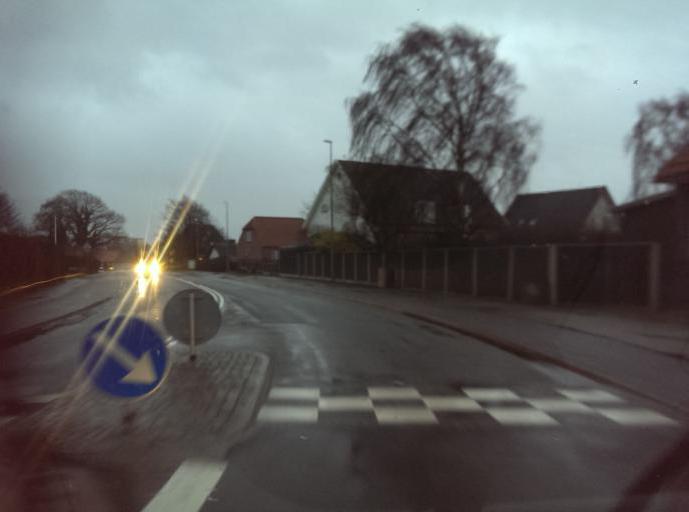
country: DK
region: South Denmark
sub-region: Esbjerg Kommune
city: Esbjerg
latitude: 55.4820
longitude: 8.4548
